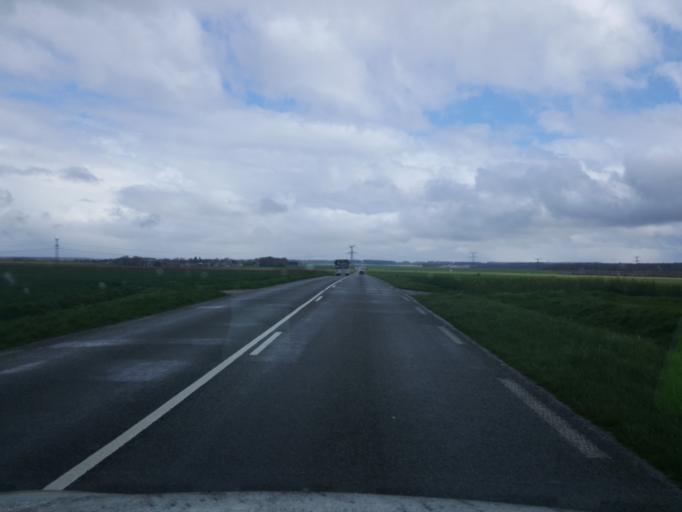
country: FR
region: Picardie
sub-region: Departement de l'Oise
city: Chaumont-en-Vexin
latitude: 49.3094
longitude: 1.8748
